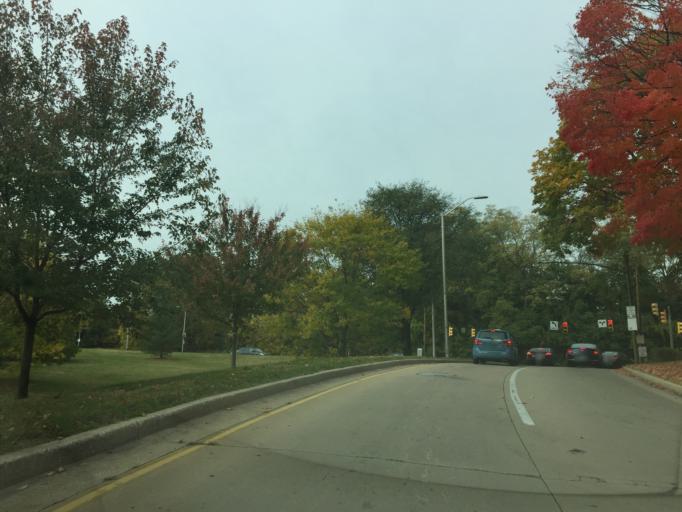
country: US
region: Maryland
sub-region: Baltimore County
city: Parkville
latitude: 39.3556
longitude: -76.5737
